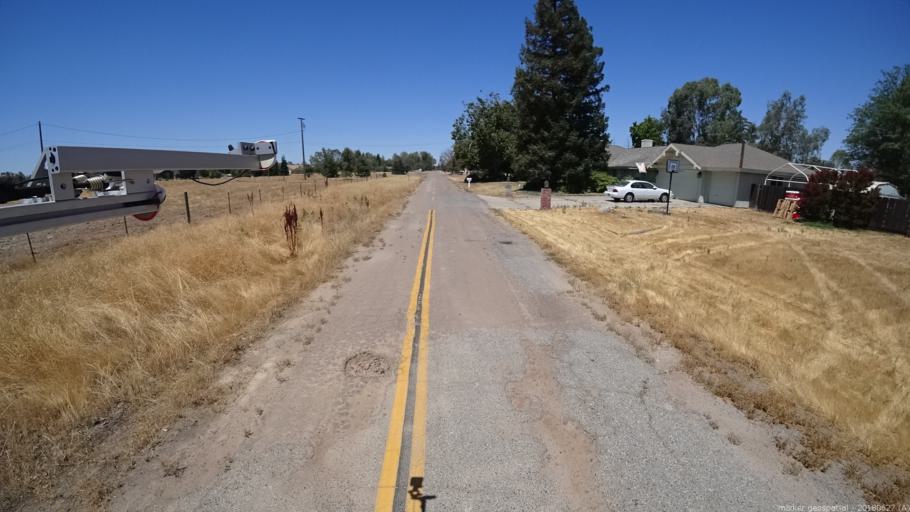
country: US
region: California
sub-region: Madera County
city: Bonadelle Ranchos-Madera Ranchos
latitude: 36.9358
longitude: -119.8584
